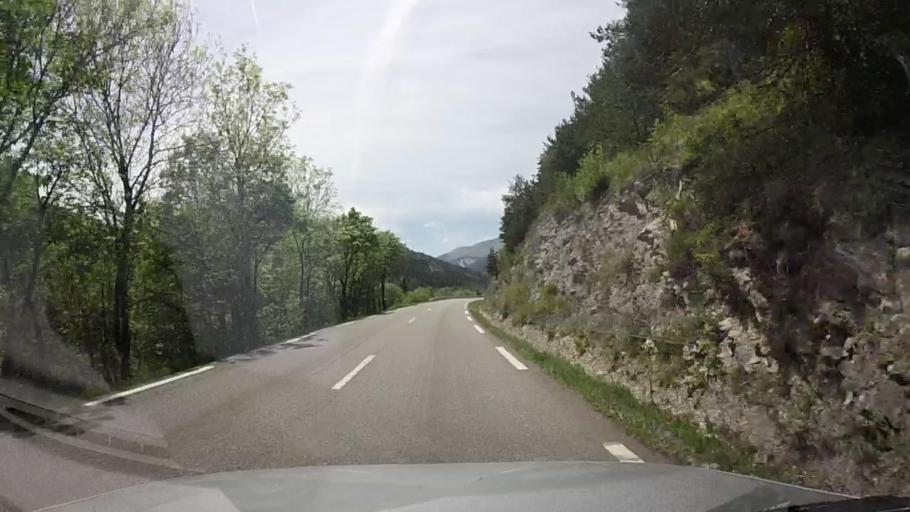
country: FR
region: Provence-Alpes-Cote d'Azur
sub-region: Departement des Alpes-de-Haute-Provence
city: Seyne-les-Alpes
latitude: 44.2737
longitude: 6.3854
